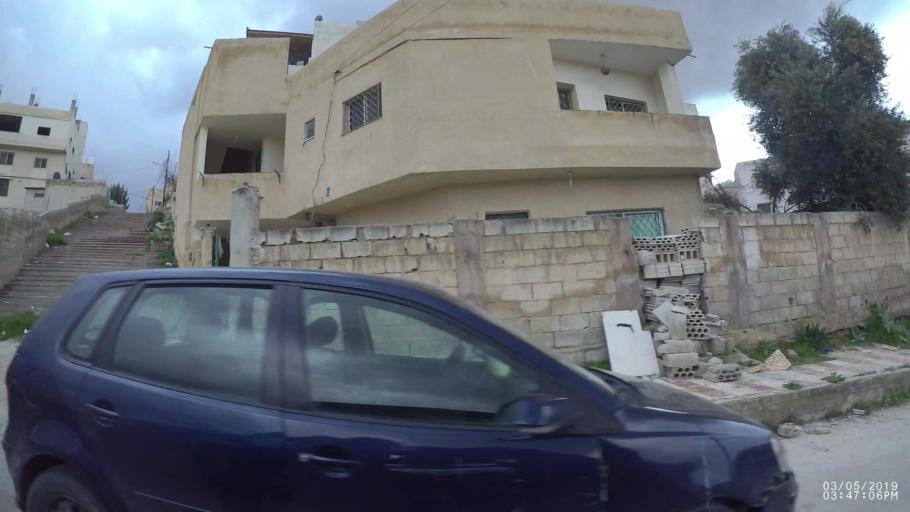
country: JO
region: Amman
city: Amman
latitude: 32.0115
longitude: 35.9509
